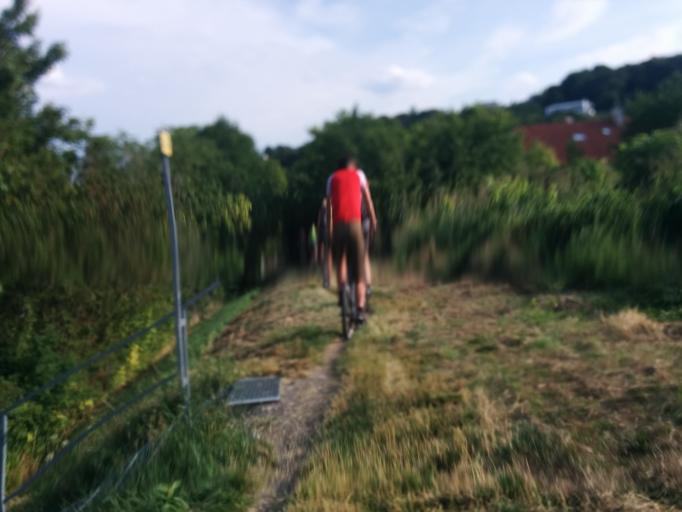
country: AT
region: Lower Austria
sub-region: Politischer Bezirk Modling
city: Modling
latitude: 48.0730
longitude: 16.2838
